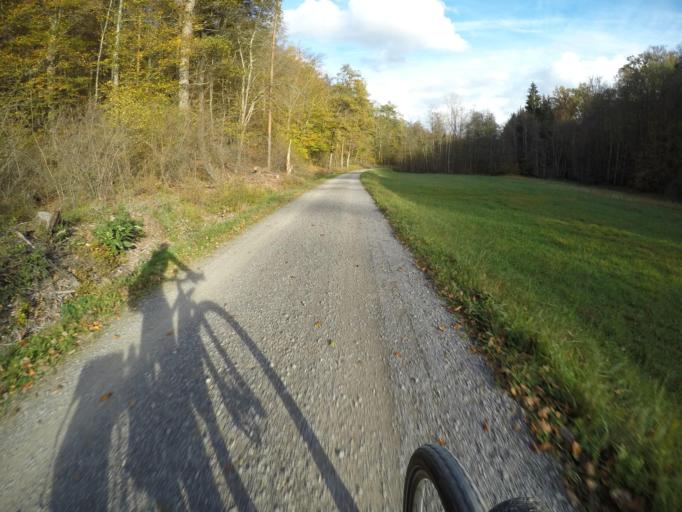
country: DE
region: Baden-Wuerttemberg
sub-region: Regierungsbezirk Stuttgart
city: Steinenbronn
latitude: 48.7016
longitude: 9.0920
